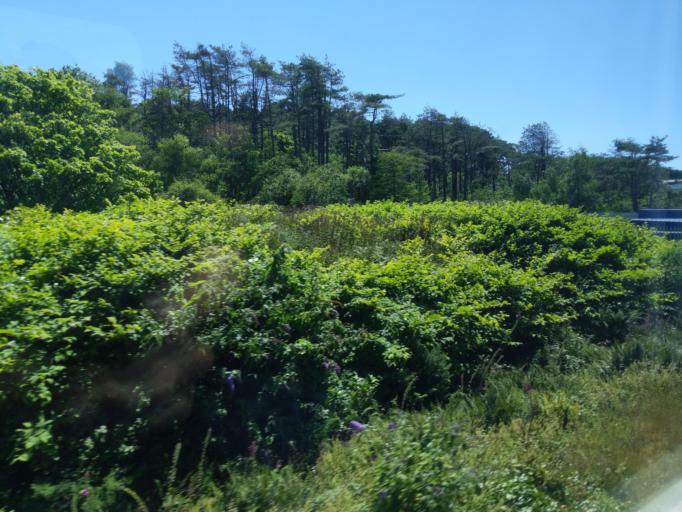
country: GB
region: England
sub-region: Cornwall
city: St. Day
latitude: 50.2510
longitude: -5.2044
